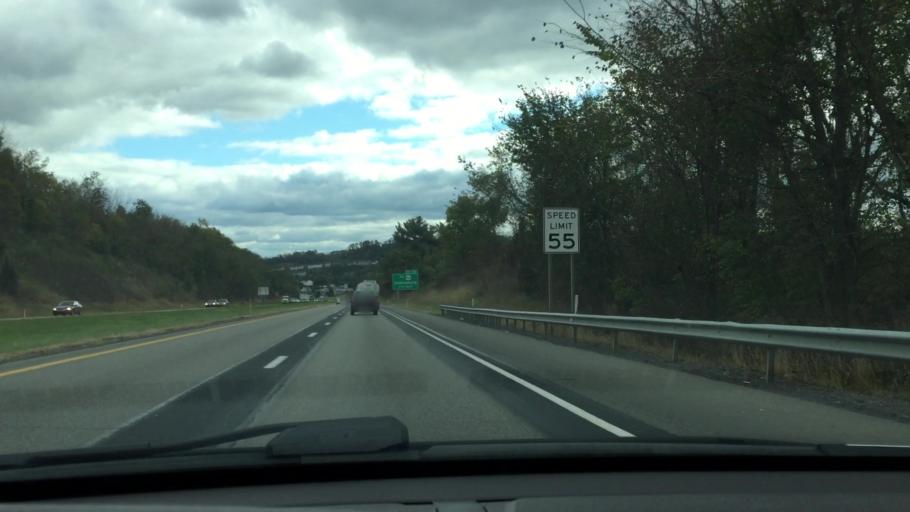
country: US
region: Pennsylvania
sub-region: Washington County
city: Canonsburg
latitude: 40.2857
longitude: -80.1674
